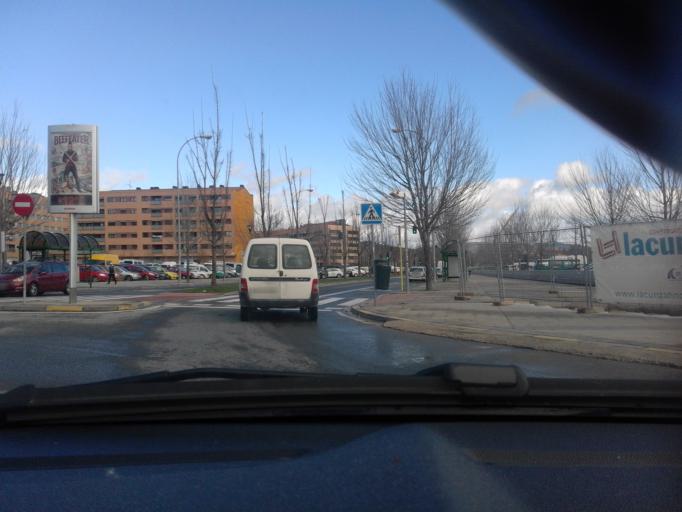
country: ES
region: Navarre
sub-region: Provincia de Navarra
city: Primer Ensanche
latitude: 42.8212
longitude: -1.6489
